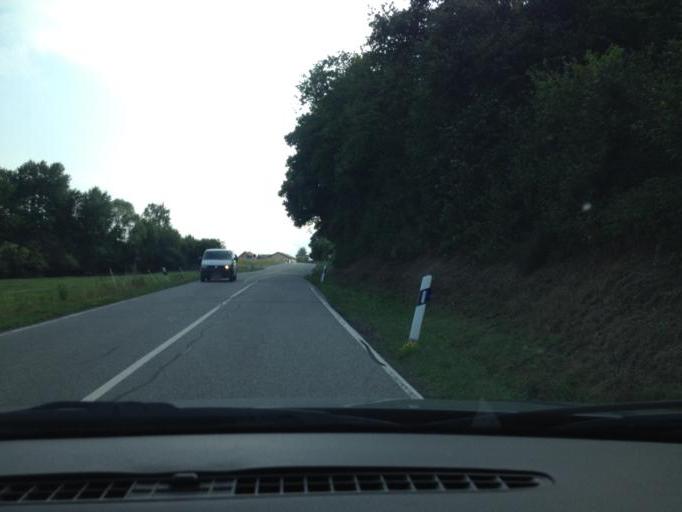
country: DE
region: Rheinland-Pfalz
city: Achtelsbach
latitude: 49.5829
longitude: 7.0703
